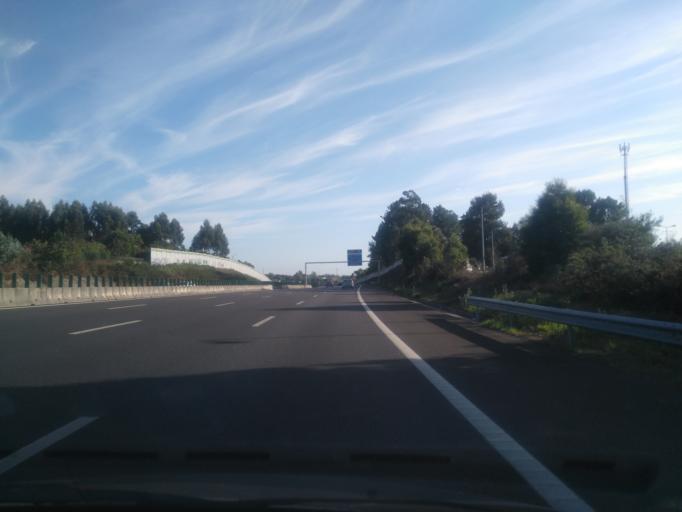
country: PT
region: Porto
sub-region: Vila Nova de Gaia
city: Grijo
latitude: 41.0382
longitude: -8.5706
